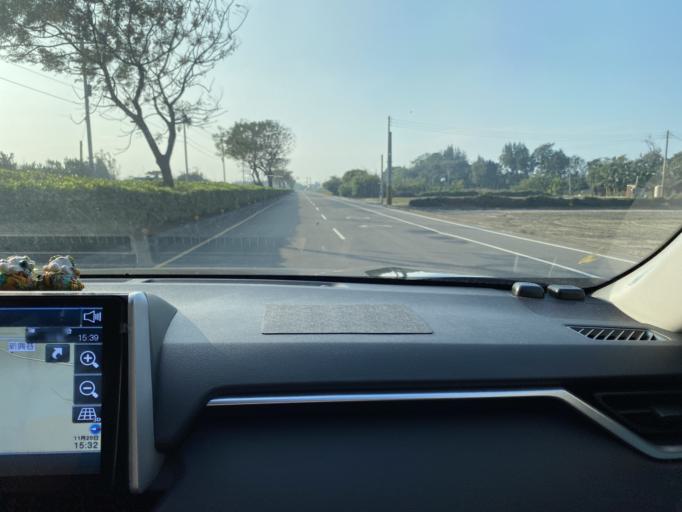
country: TW
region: Taiwan
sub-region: Changhua
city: Chang-hua
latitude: 23.9604
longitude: 120.3941
